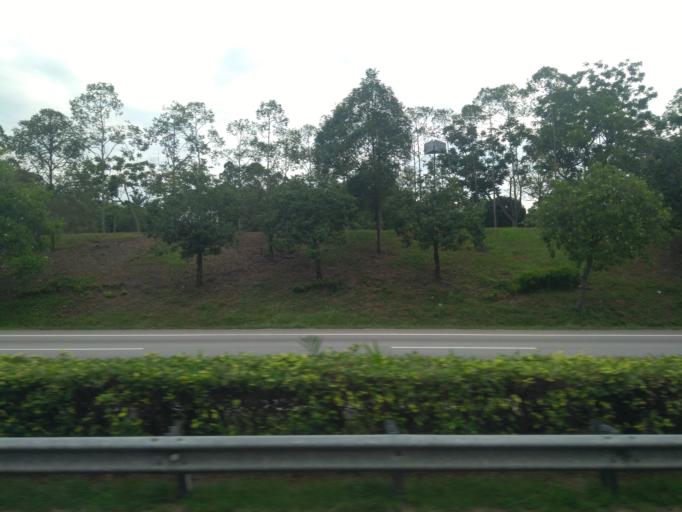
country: MY
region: Melaka
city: Alor Gajah
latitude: 2.3964
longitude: 102.2219
